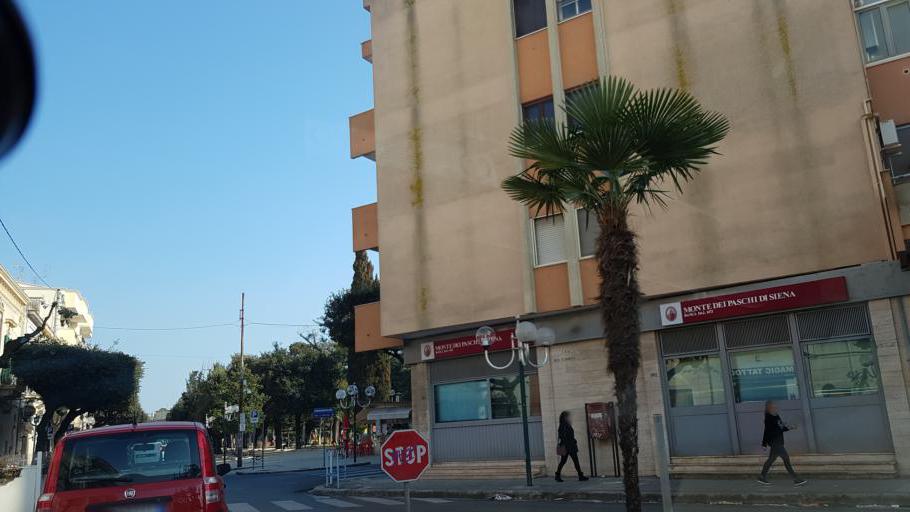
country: IT
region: Apulia
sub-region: Provincia di Brindisi
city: Mesagne
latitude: 40.5620
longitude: 17.8049
